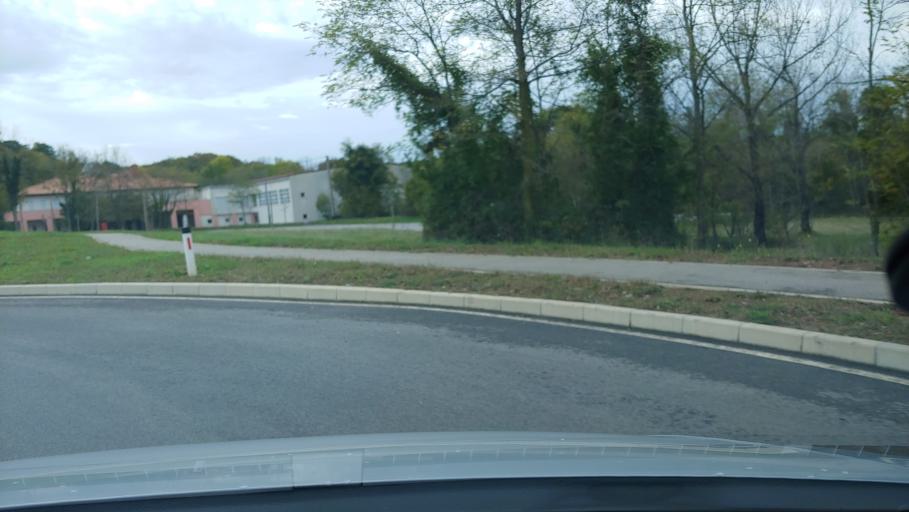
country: SI
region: Komen
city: Komen
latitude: 45.8215
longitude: 13.7521
